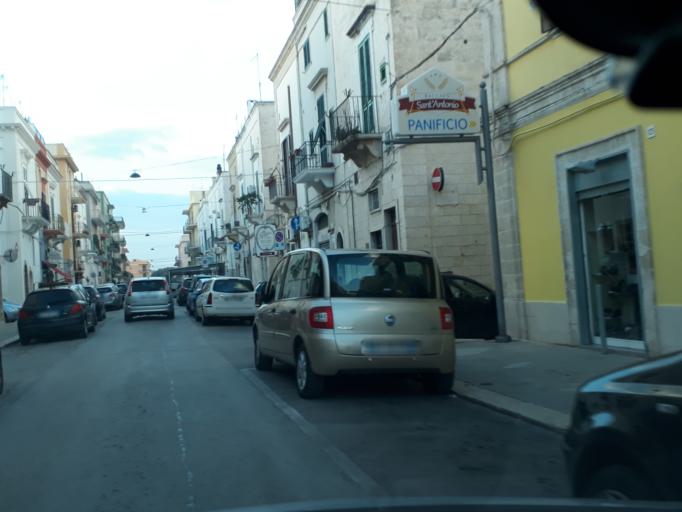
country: IT
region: Apulia
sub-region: Provincia di Brindisi
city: Fasano
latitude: 40.8375
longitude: 17.3564
